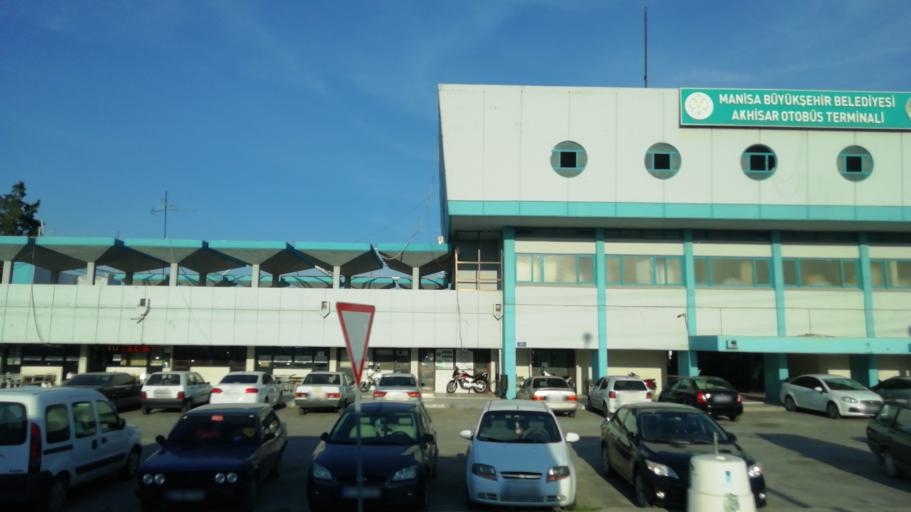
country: TR
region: Manisa
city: Akhisar
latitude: 38.9340
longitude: 27.8349
